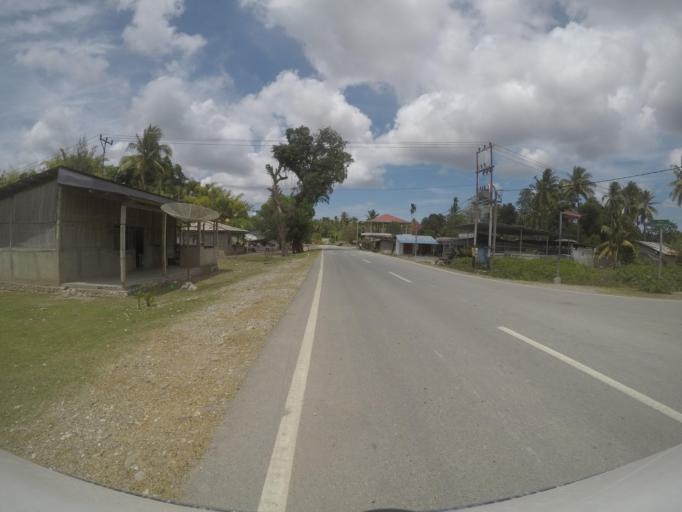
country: TL
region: Viqueque
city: Viqueque
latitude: -8.8821
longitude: 126.3758
